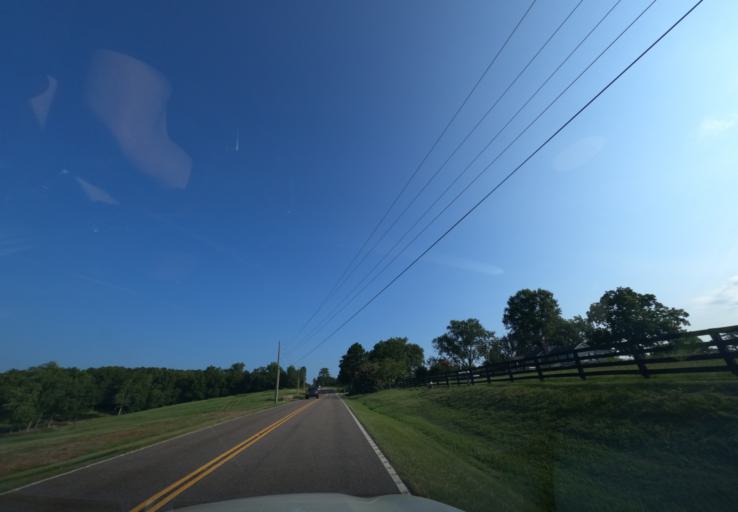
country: US
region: South Carolina
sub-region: Edgefield County
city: Murphys Estates
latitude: 33.6643
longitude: -81.9754
